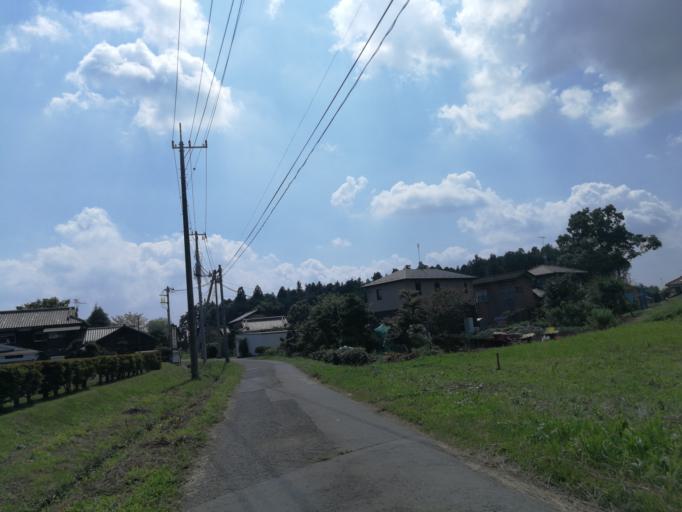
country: JP
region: Ibaraki
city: Tomobe
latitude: 36.3697
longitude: 140.3430
